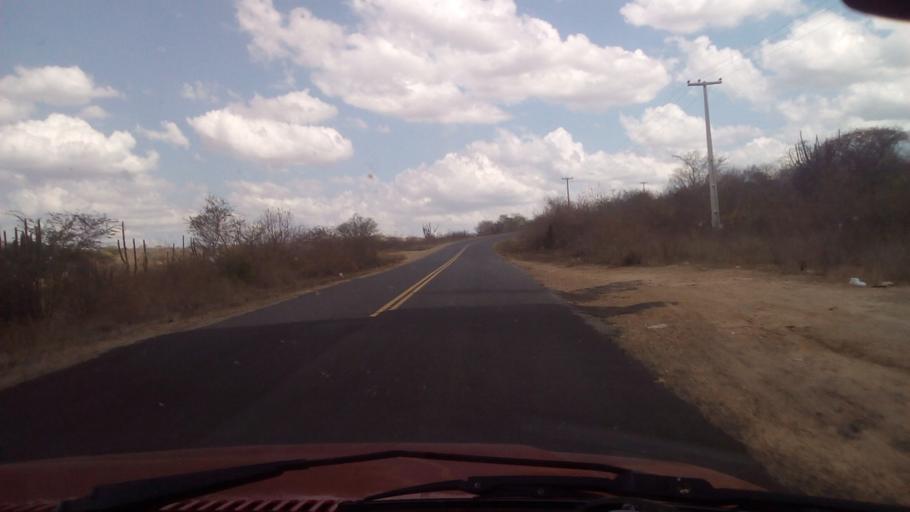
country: BR
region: Paraiba
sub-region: Cacimba De Dentro
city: Cacimba de Dentro
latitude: -6.6914
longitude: -35.7433
